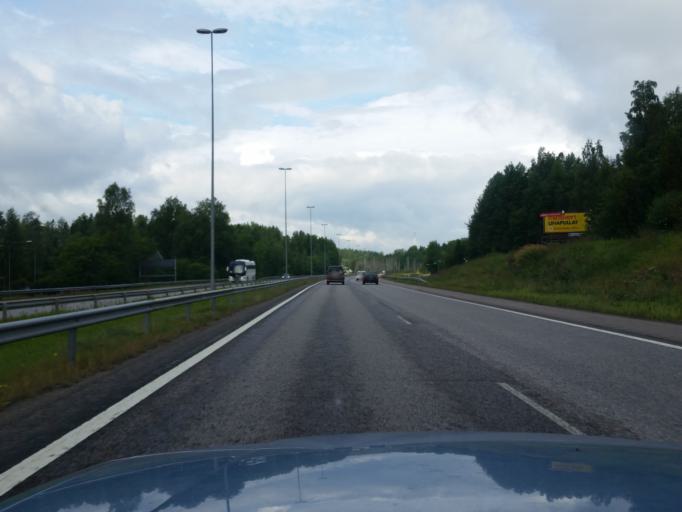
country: FI
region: Uusimaa
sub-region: Helsinki
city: Kirkkonummi
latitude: 60.2820
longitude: 24.4395
